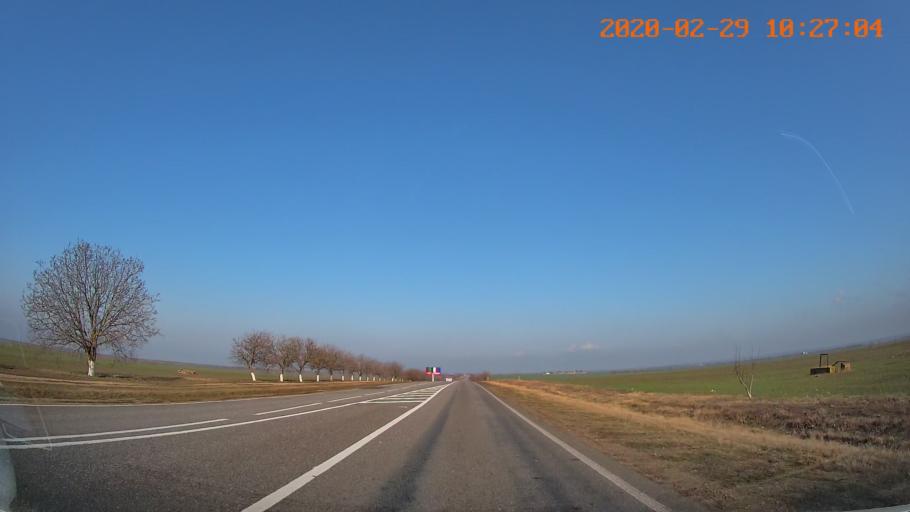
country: MD
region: Telenesti
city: Tiraspolul Nou
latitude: 46.8910
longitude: 29.6000
